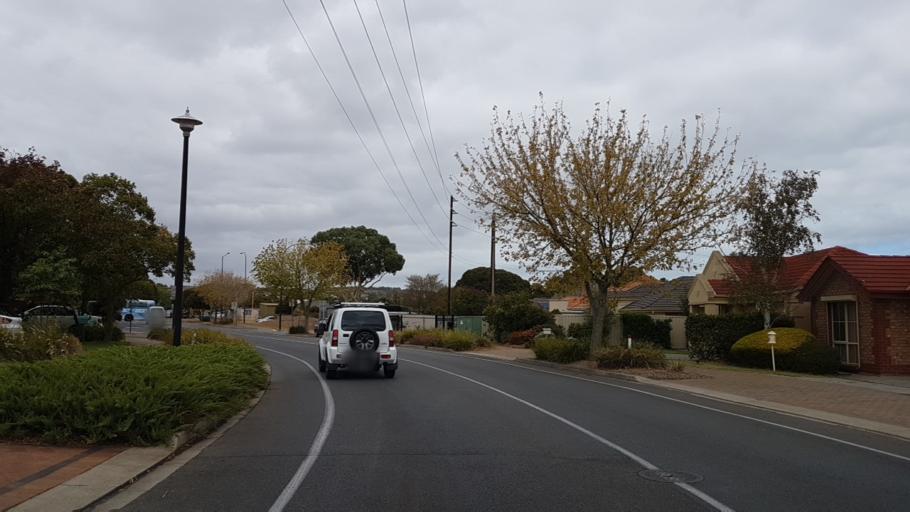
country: AU
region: South Australia
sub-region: Marion
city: Marion
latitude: -35.0158
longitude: 138.5644
